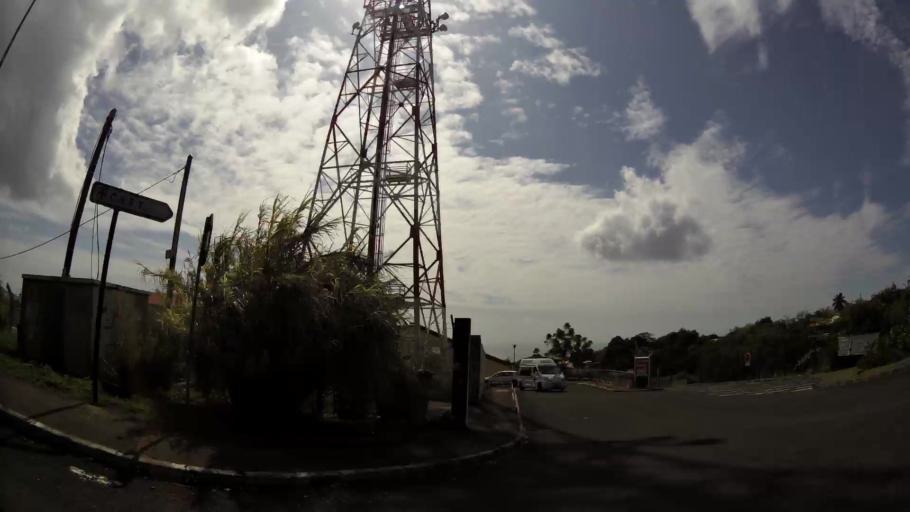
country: GP
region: Guadeloupe
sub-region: Guadeloupe
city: Basse-Terre
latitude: 16.0049
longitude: -61.7300
